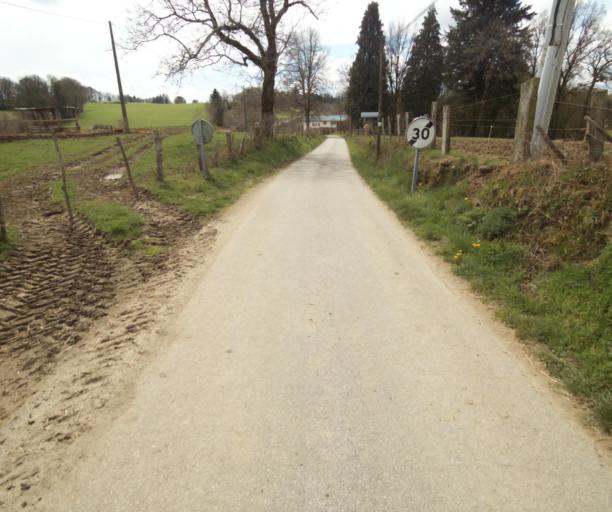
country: FR
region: Limousin
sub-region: Departement de la Correze
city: Correze
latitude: 45.3868
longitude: 1.9621
